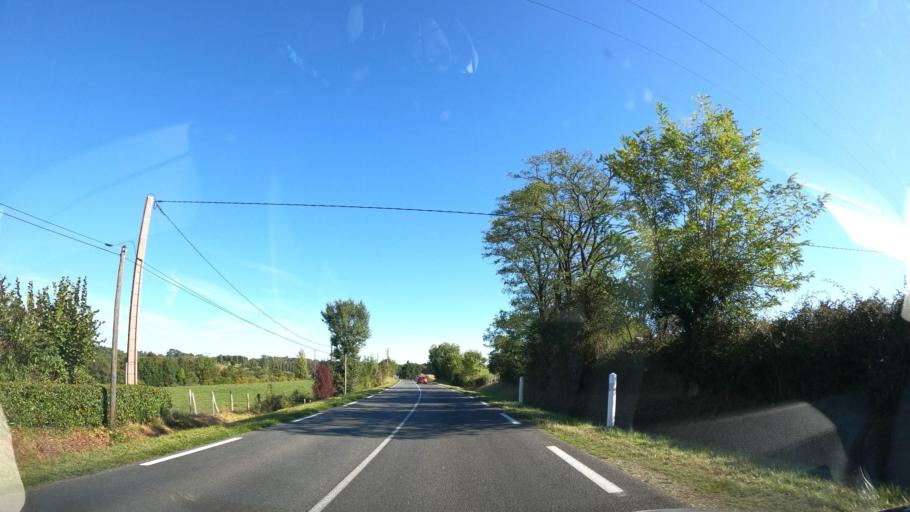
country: FR
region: Aquitaine
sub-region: Departement de la Dordogne
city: Lembras
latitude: 44.9541
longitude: 0.5837
